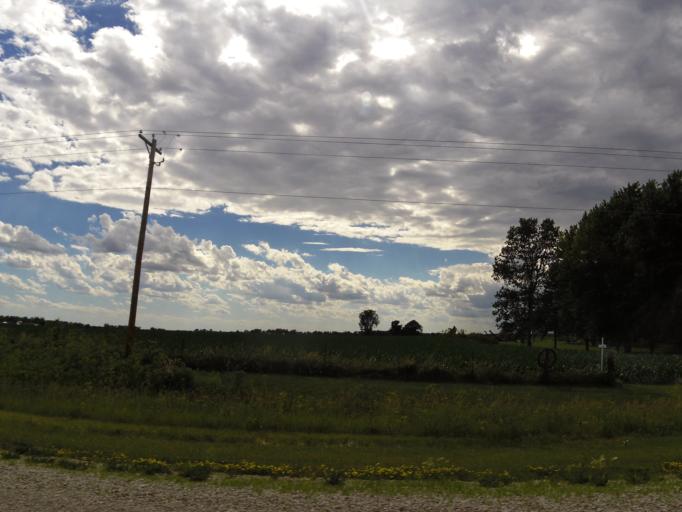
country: US
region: Iowa
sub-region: Henry County
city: Mount Pleasant
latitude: 40.7581
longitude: -91.5642
